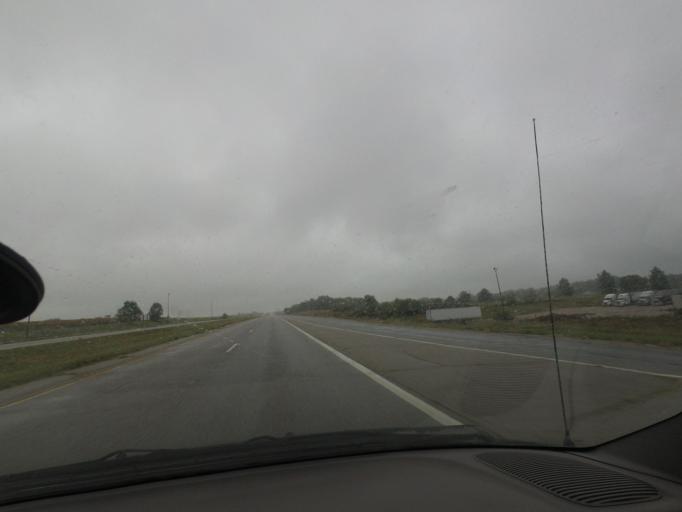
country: US
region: Illinois
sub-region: Pike County
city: Barry
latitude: 39.7037
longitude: -91.0368
